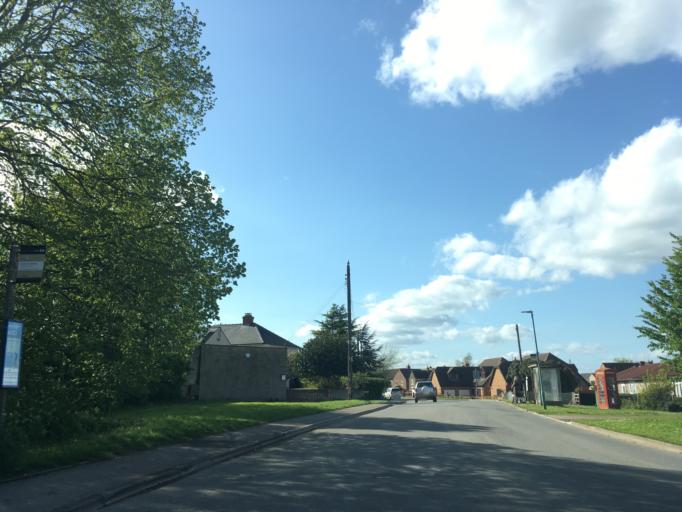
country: GB
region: England
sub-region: Gloucestershire
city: Stonehouse
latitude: 51.7314
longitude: -2.2796
